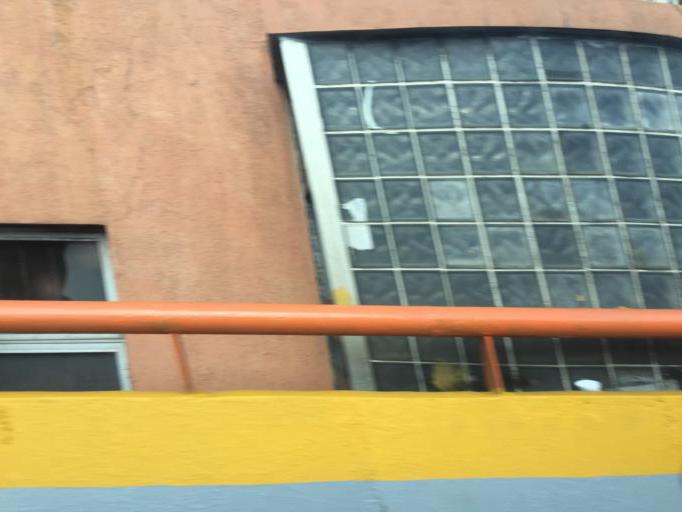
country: DO
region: Nacional
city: San Carlos
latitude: 18.4836
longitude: -69.8918
